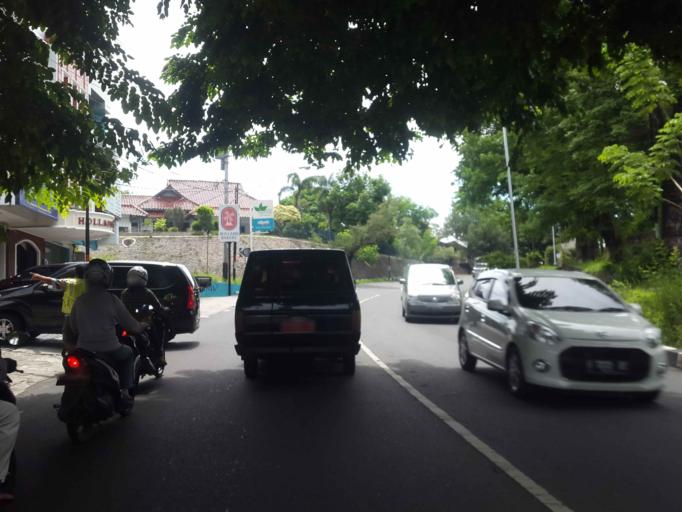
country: ID
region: Central Java
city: Semarang
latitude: -7.0005
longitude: 110.4202
